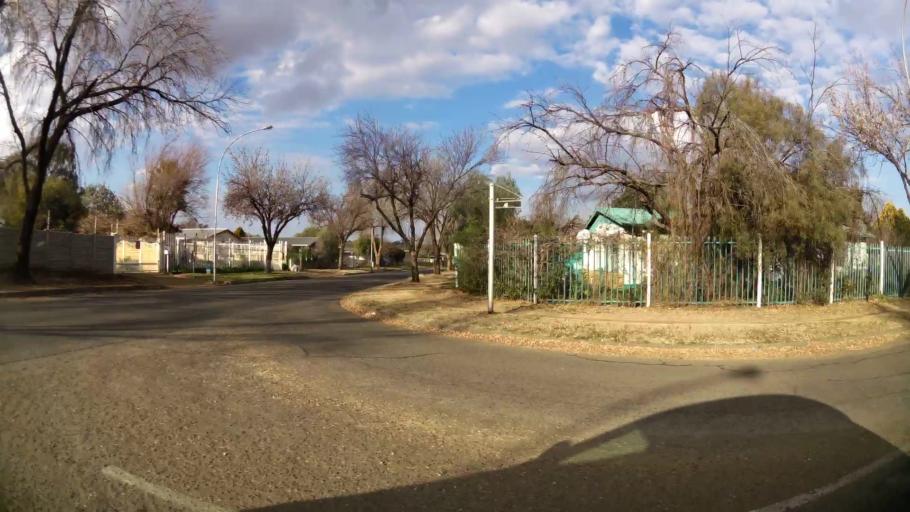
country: ZA
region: Orange Free State
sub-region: Mangaung Metropolitan Municipality
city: Bloemfontein
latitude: -29.0992
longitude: 26.1929
